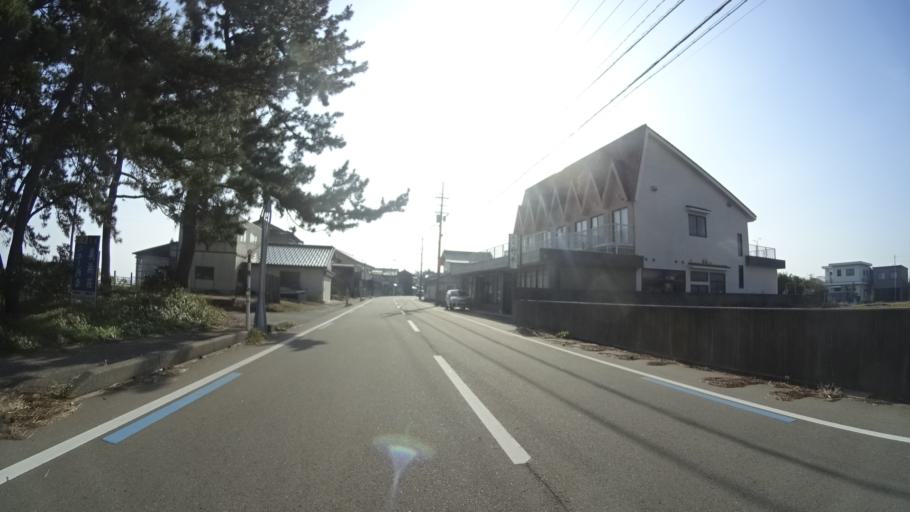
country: JP
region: Toyama
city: Himi
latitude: 36.8325
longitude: 137.0112
